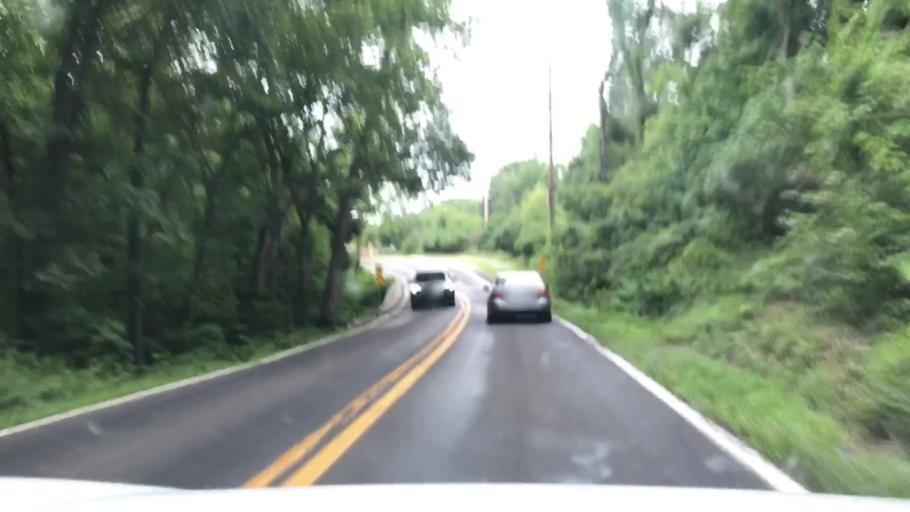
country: US
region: Missouri
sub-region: Saint Louis County
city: Clarkson Valley
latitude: 38.6487
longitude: -90.6159
